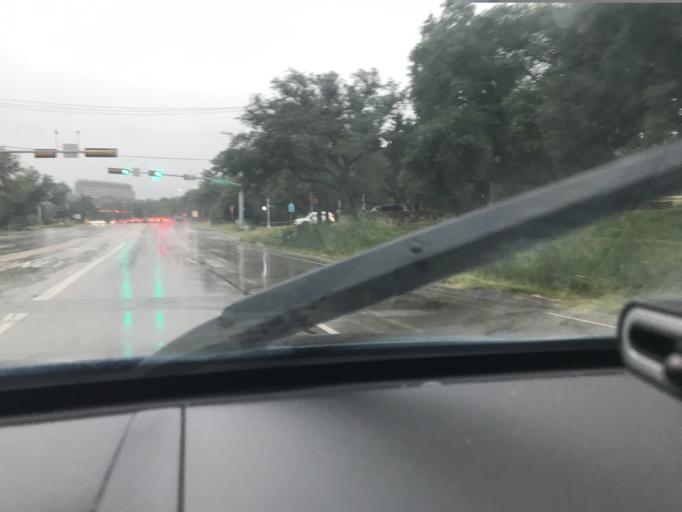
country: US
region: Texas
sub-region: Travis County
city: West Lake Hills
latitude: 30.2924
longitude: -97.8222
